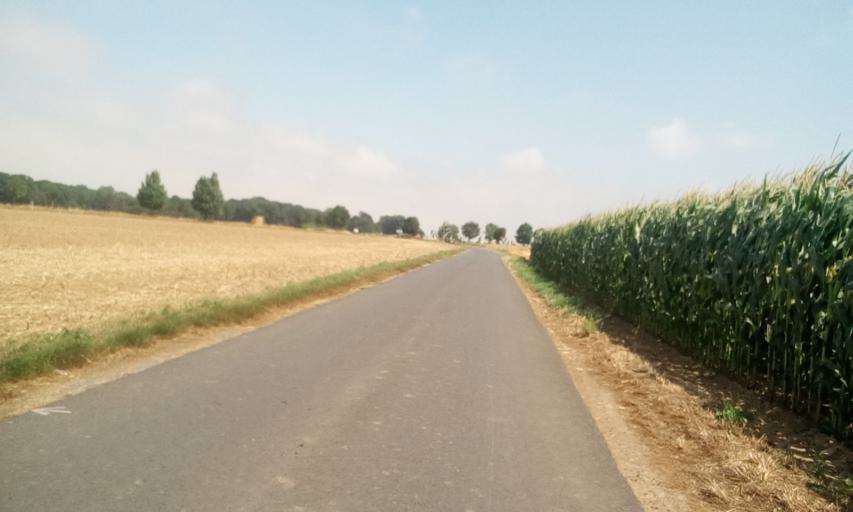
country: FR
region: Lower Normandy
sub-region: Departement du Calvados
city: Bernieres-sur-Mer
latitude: 49.2908
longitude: -0.4224
